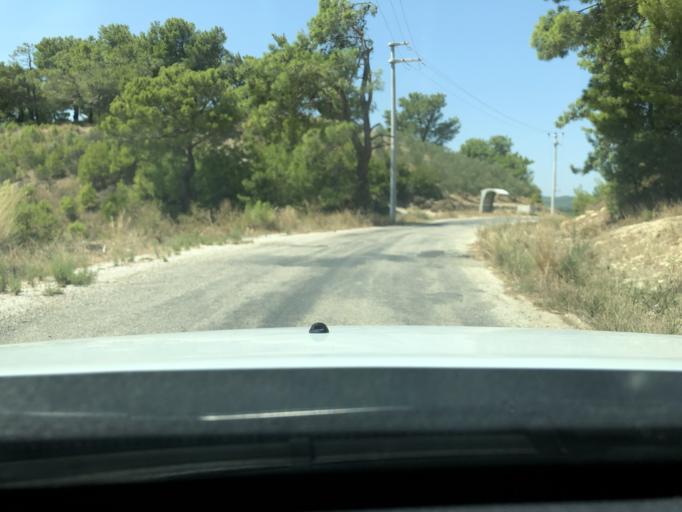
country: TR
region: Antalya
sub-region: Manavgat
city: Kizilagac
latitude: 36.8640
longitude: 31.5616
